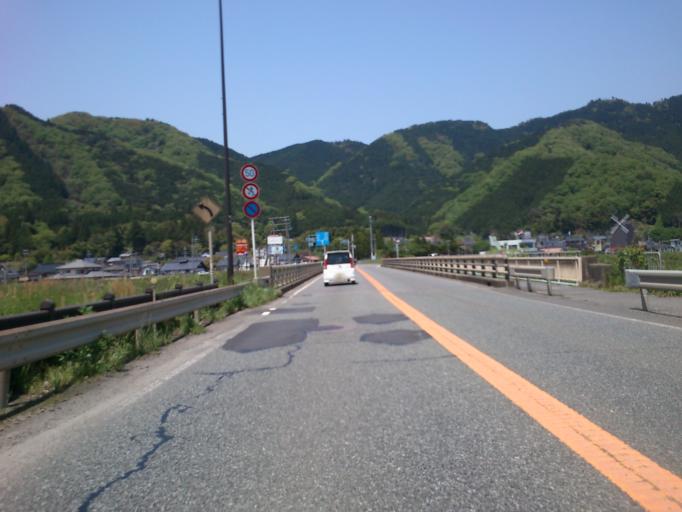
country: JP
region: Kyoto
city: Fukuchiyama
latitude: 35.3331
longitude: 135.0988
